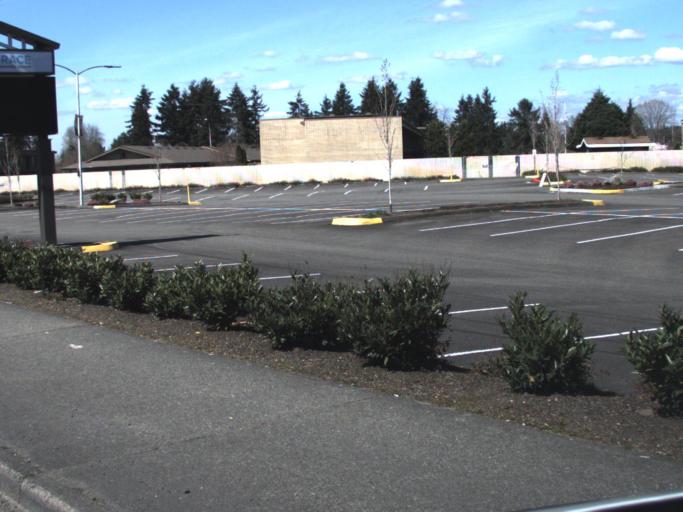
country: US
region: Washington
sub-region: King County
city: Auburn
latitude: 47.2958
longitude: -122.2155
